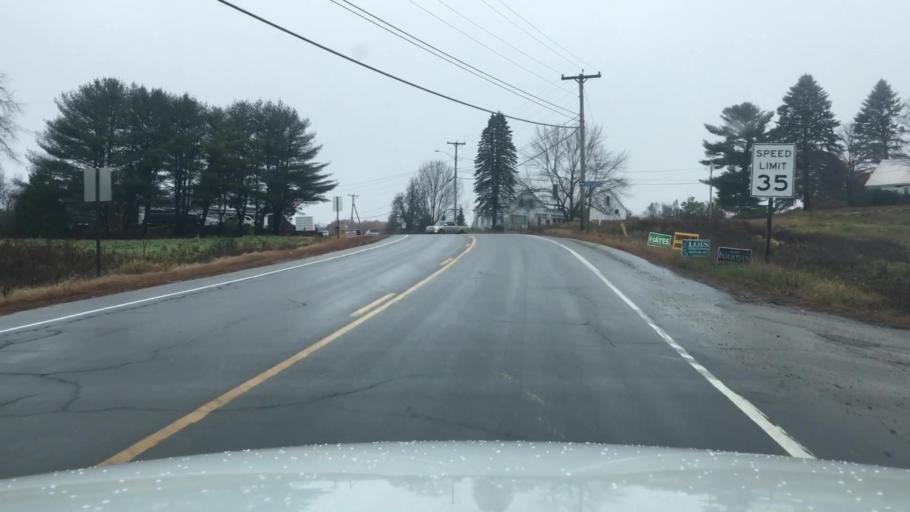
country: US
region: Maine
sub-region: Androscoggin County
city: Sabattus
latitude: 44.1101
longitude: -70.0902
